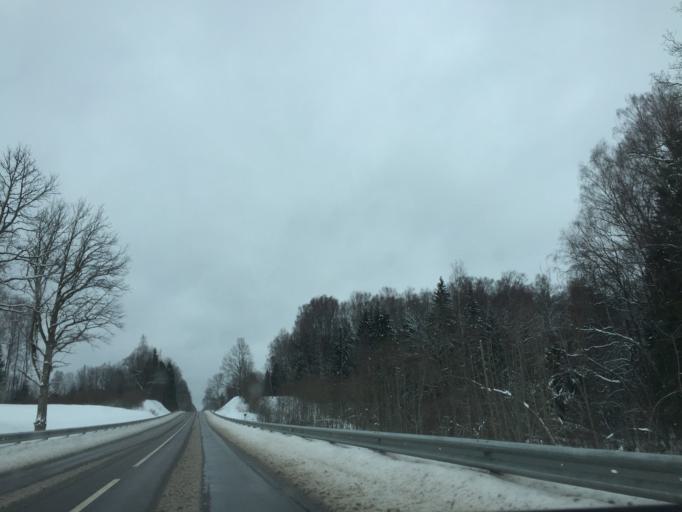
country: LV
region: Ligatne
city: Ligatne
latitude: 57.1318
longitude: 25.0862
